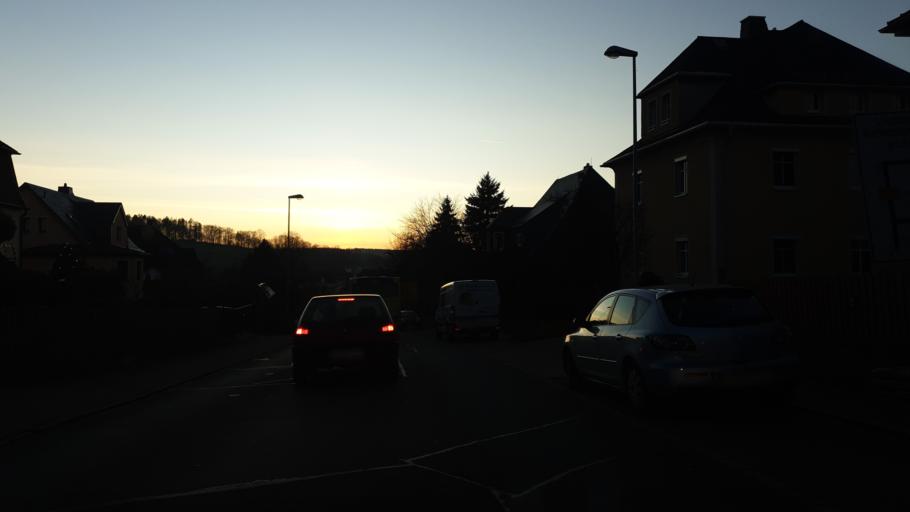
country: DE
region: Saxony
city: Hohndorf
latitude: 50.7475
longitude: 12.6712
